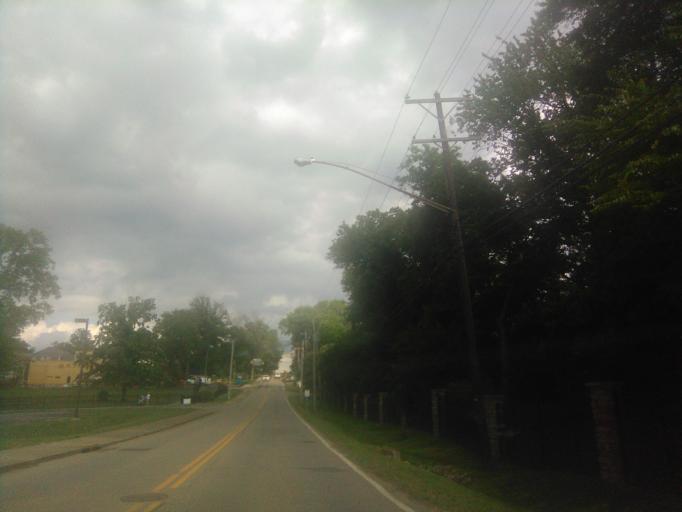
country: US
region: Tennessee
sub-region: Davidson County
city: Belle Meade
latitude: 36.1022
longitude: -86.8321
